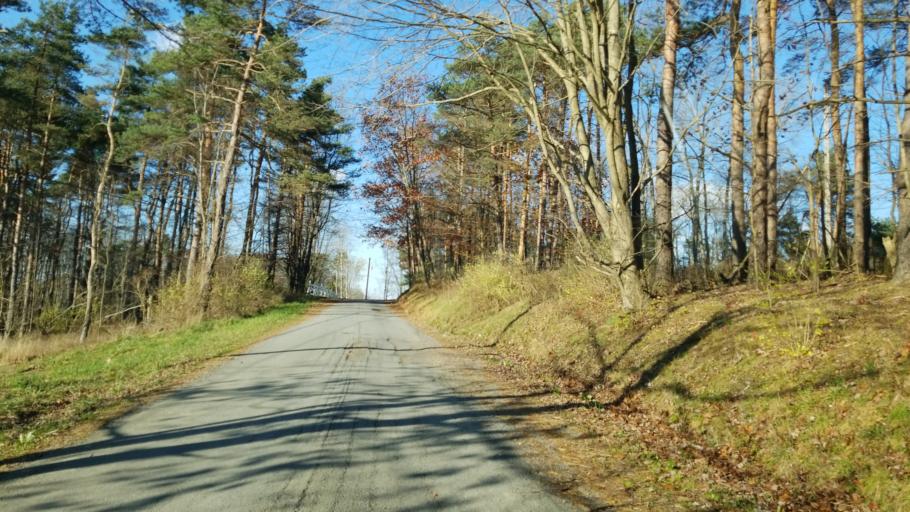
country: US
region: Pennsylvania
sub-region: Clearfield County
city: Treasure Lake
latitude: 41.1539
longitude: -78.6608
